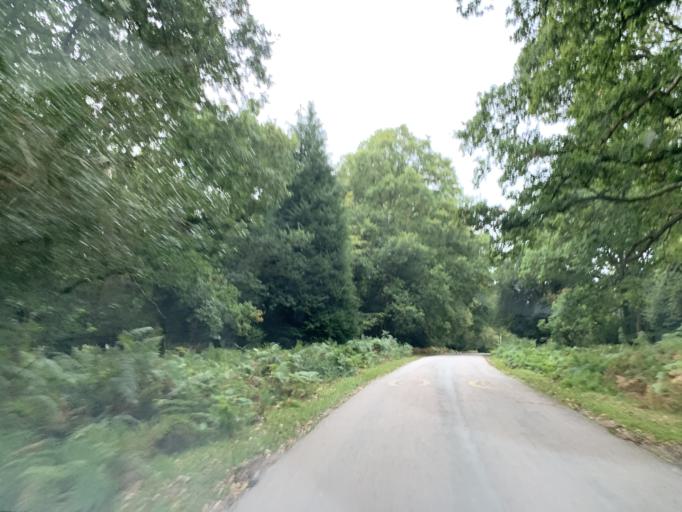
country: GB
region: England
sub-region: Hampshire
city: Brockenhurst
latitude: 50.8385
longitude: -1.6227
